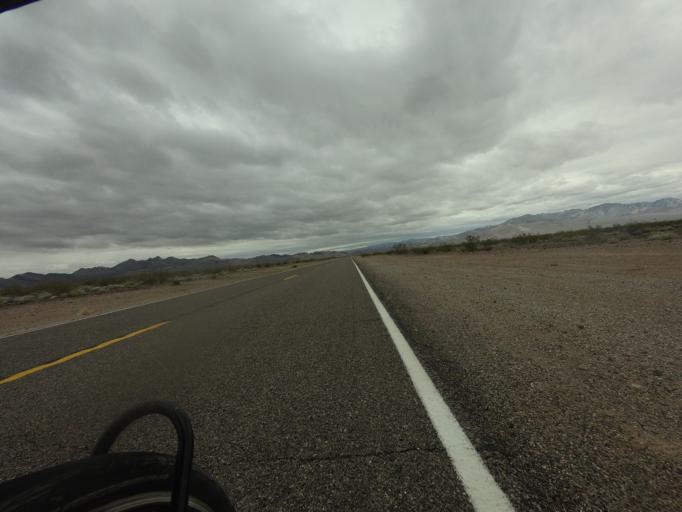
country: US
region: Nevada
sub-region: Nye County
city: Beatty
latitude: 36.8373
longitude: -116.8738
